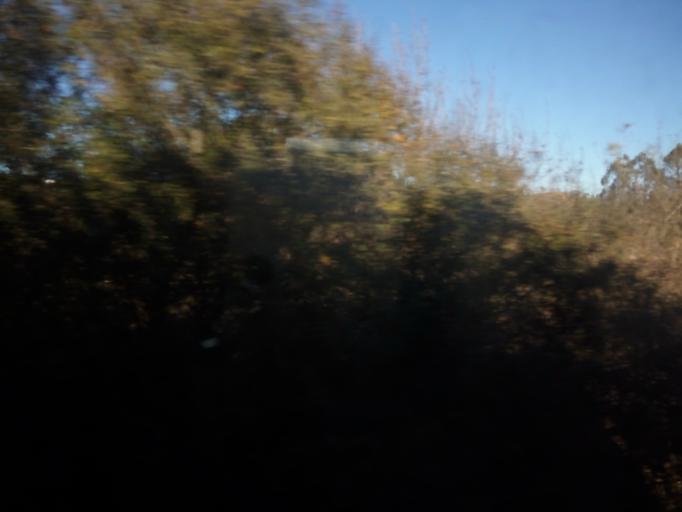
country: PT
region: Faro
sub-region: Silves
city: Sao Bartolomeu de Messines
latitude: 37.3357
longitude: -8.3475
